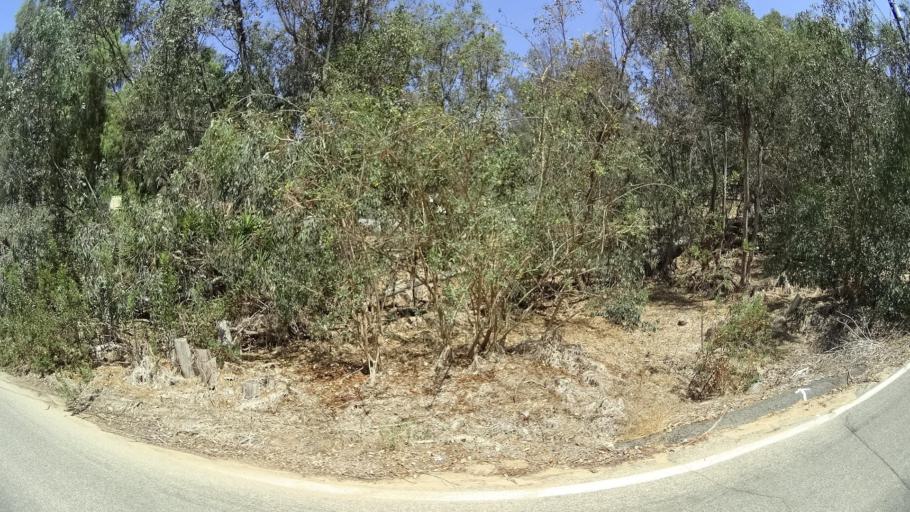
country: US
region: California
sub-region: San Diego County
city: Bonsall
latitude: 33.2687
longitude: -117.2131
